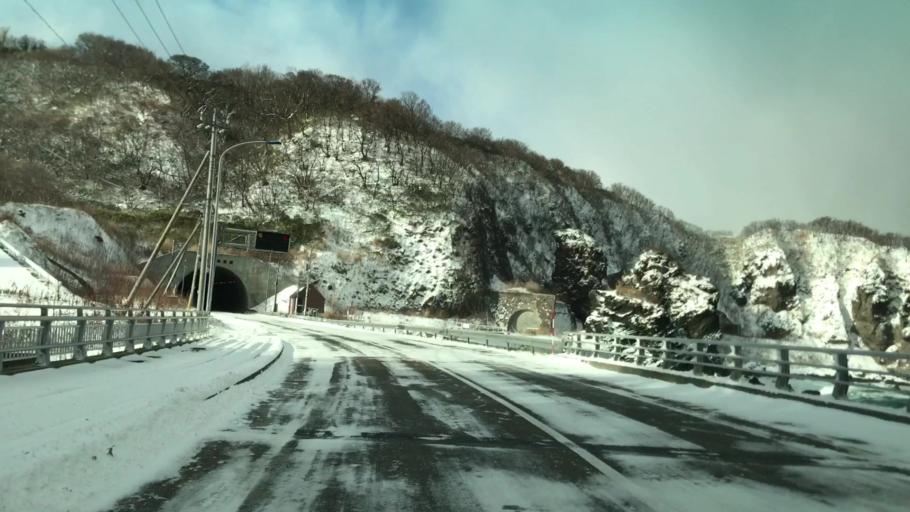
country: JP
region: Hokkaido
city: Iwanai
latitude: 43.3325
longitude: 140.4105
